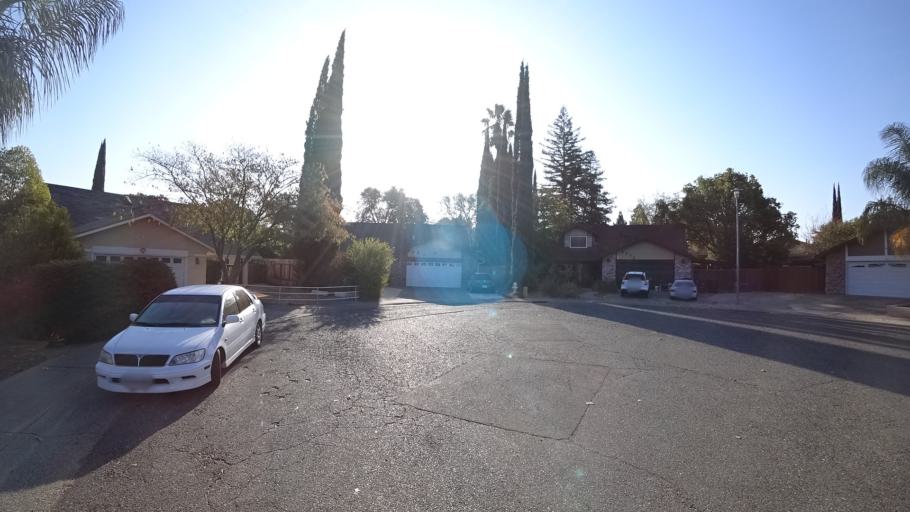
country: US
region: California
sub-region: Sacramento County
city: Citrus Heights
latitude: 38.6972
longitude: -121.2654
